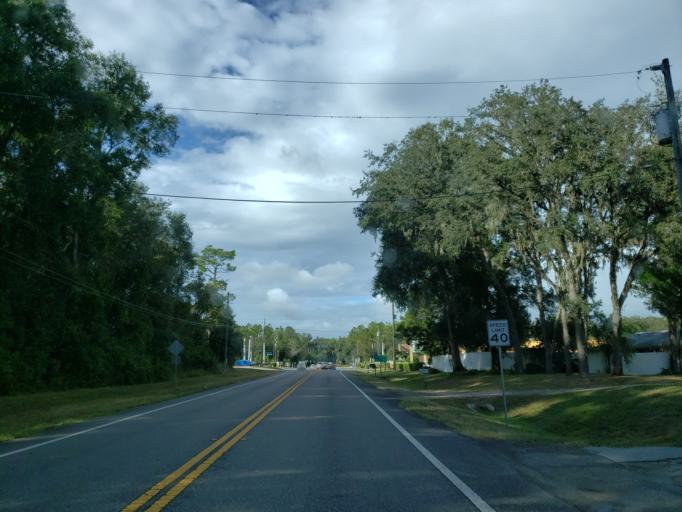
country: US
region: Florida
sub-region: Hernando County
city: Hill 'n Dale
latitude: 28.5214
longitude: -82.3032
